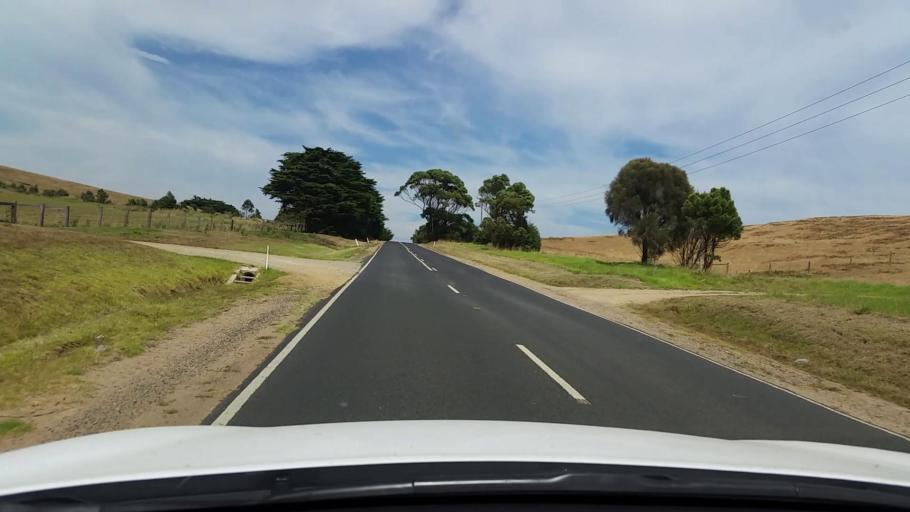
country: AU
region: Victoria
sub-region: Mornington Peninsula
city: Merricks
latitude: -38.4756
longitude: 144.9957
